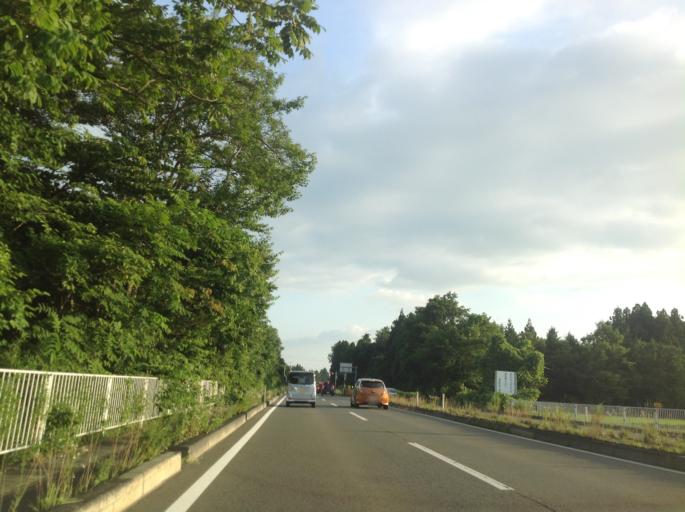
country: JP
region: Iwate
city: Hanamaki
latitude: 39.4812
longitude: 141.1403
